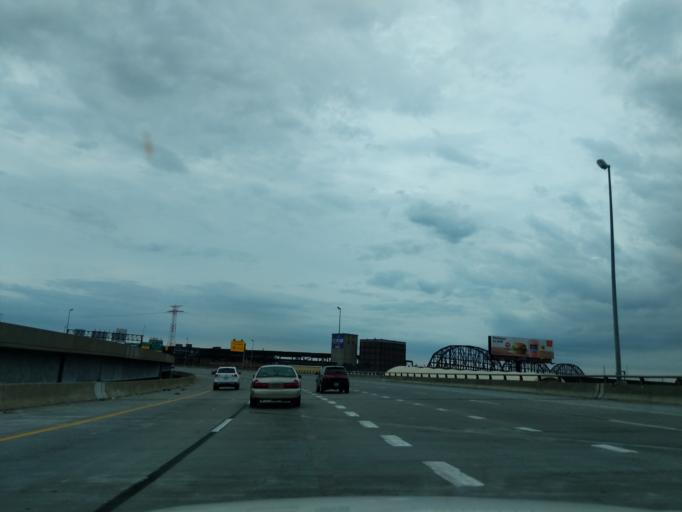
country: US
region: Missouri
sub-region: City of Saint Louis
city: St. Louis
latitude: 38.6147
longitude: -90.1927
